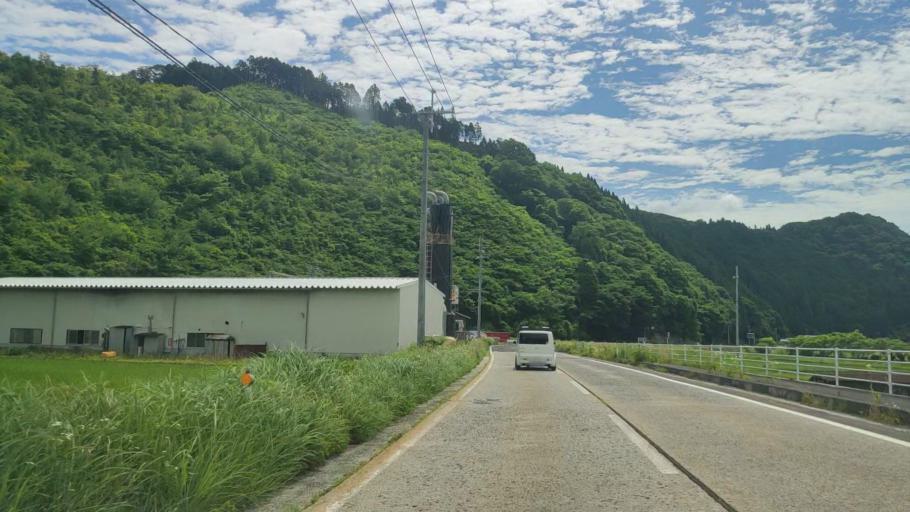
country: JP
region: Okayama
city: Niimi
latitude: 35.1726
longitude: 133.5740
